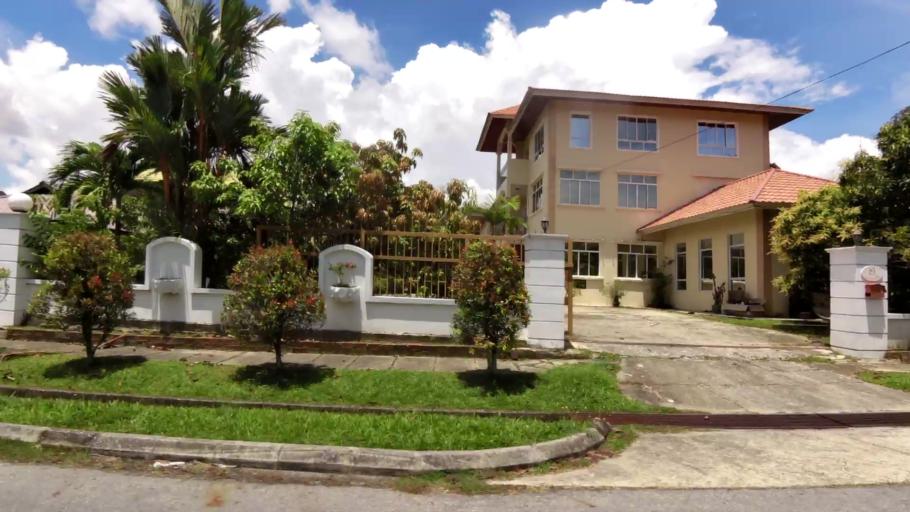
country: BN
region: Brunei and Muara
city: Bandar Seri Begawan
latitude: 4.9636
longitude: 114.9141
